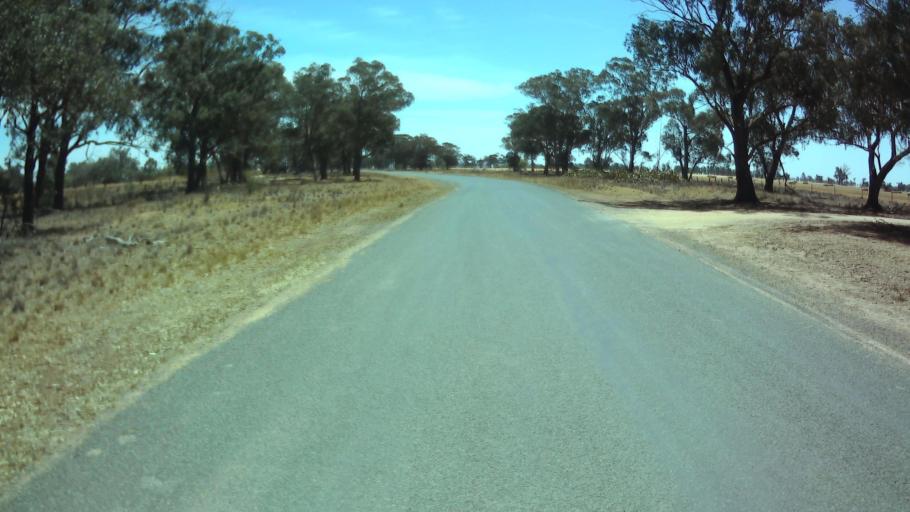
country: AU
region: New South Wales
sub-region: Weddin
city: Grenfell
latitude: -34.0087
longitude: 147.7865
